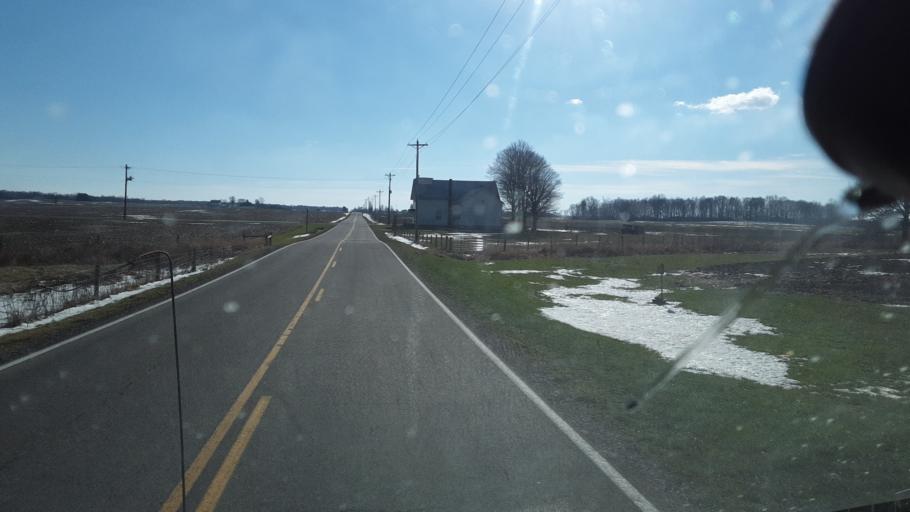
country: US
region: Ohio
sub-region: Huron County
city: Plymouth
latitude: 40.9467
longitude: -82.7433
